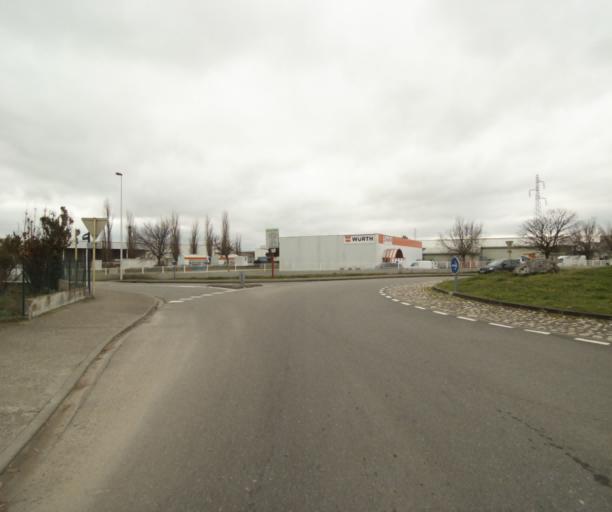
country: FR
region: Midi-Pyrenees
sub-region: Departement de l'Ariege
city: Pamiers
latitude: 43.1298
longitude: 1.6231
